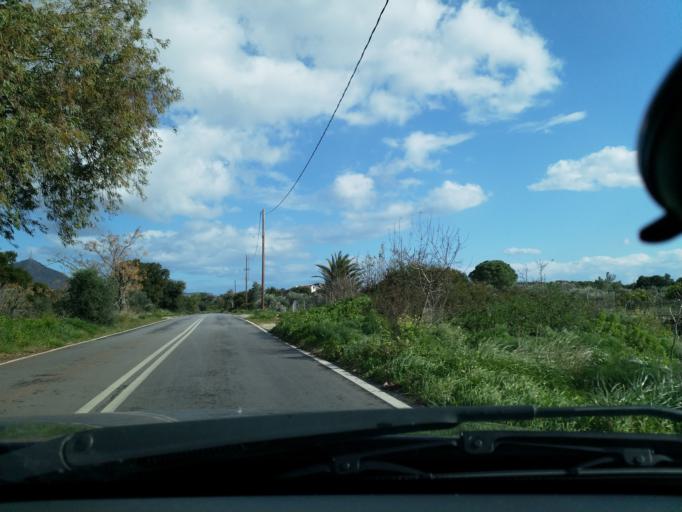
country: GR
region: Crete
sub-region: Nomos Chanias
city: Mouzouras
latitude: 35.5192
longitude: 24.1396
